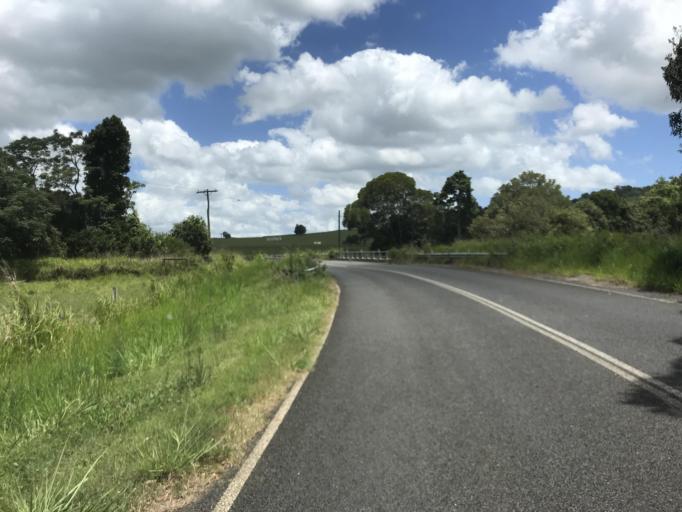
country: AU
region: Queensland
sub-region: Tablelands
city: Atherton
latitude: -17.3006
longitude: 145.5625
